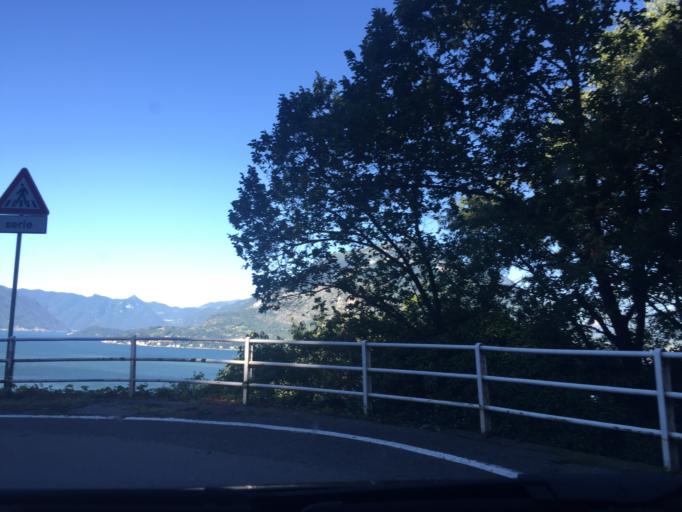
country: IT
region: Lombardy
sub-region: Provincia di Lecco
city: Perledo
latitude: 46.0176
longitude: 9.2891
